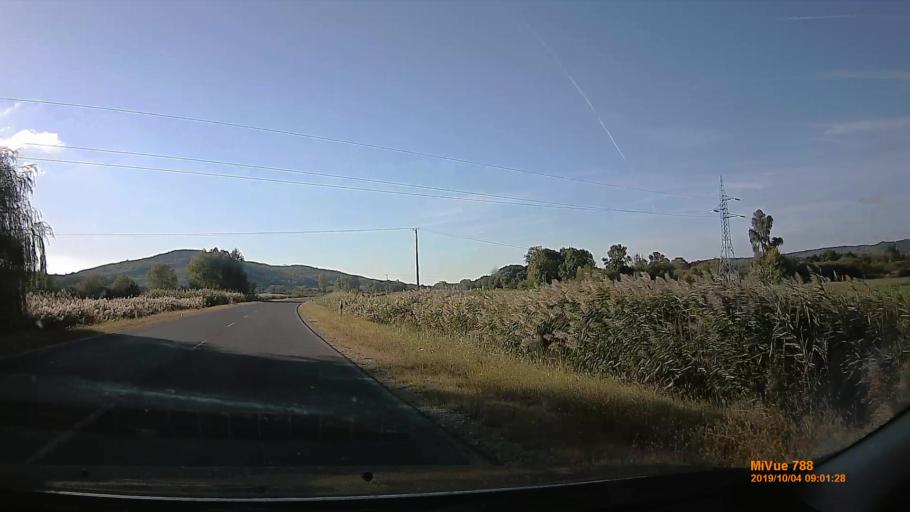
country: HU
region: Somogy
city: Karad
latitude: 46.7352
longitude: 17.7764
